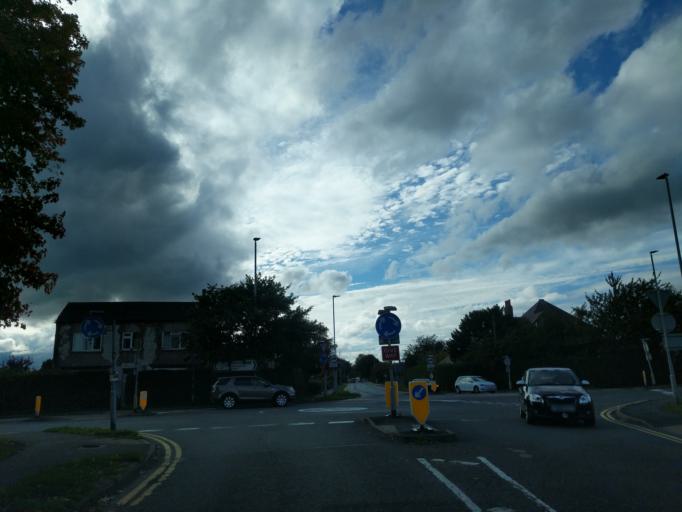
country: GB
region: England
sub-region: Leicestershire
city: Ibstock
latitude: 52.6922
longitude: -1.4018
